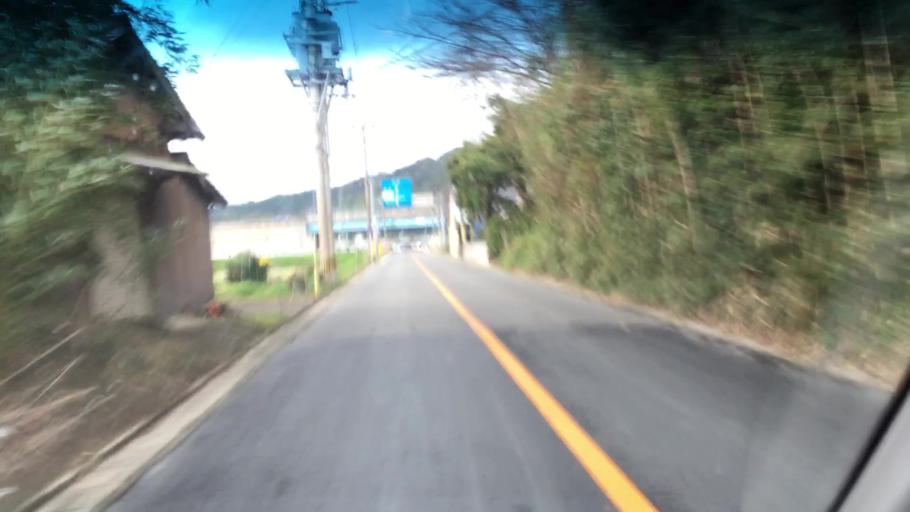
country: JP
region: Fukuoka
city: Maebaru-chuo
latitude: 33.5300
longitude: 130.1887
